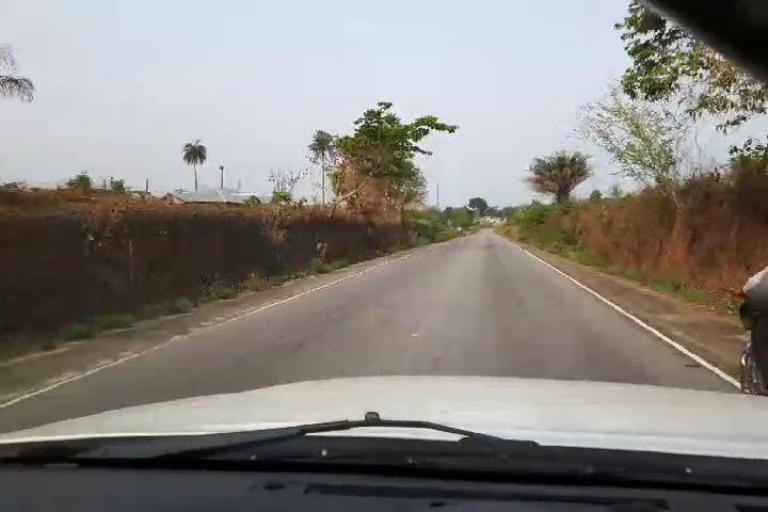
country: SL
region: Southern Province
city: Baoma
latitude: 7.9289
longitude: -11.5797
